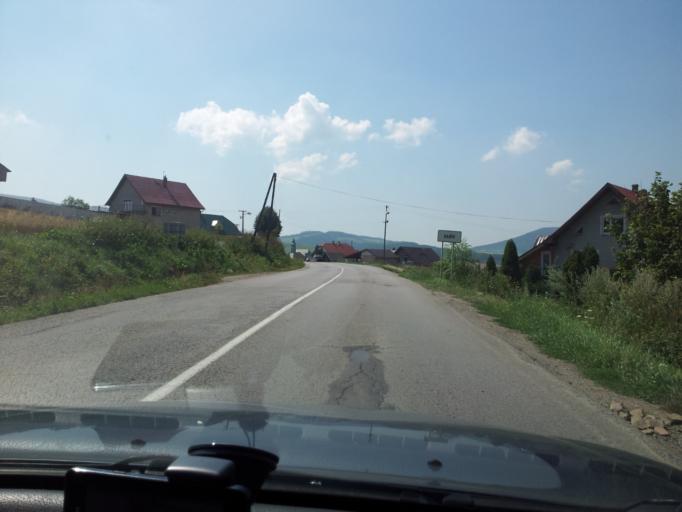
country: SK
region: Zilinsky
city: Namestovo
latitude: 49.3392
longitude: 19.3831
